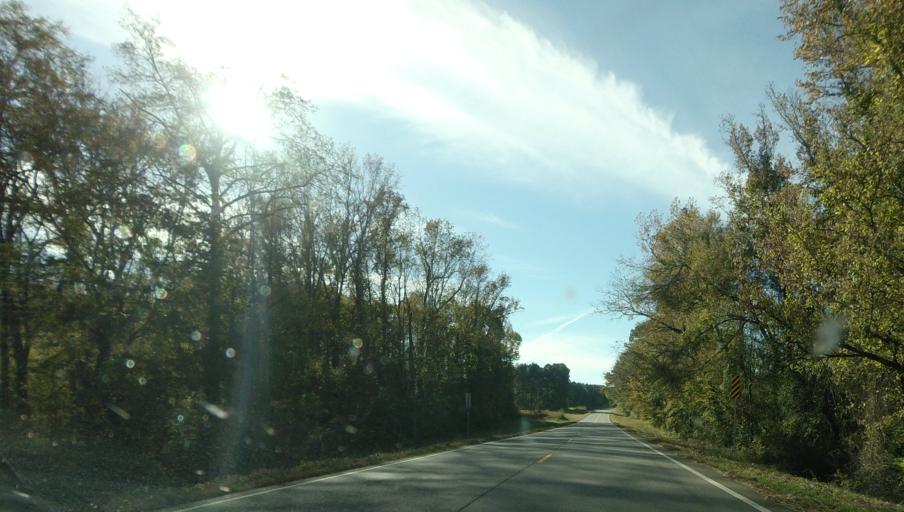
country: US
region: Georgia
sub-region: Talbot County
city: Talbotton
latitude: 32.6888
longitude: -84.4830
